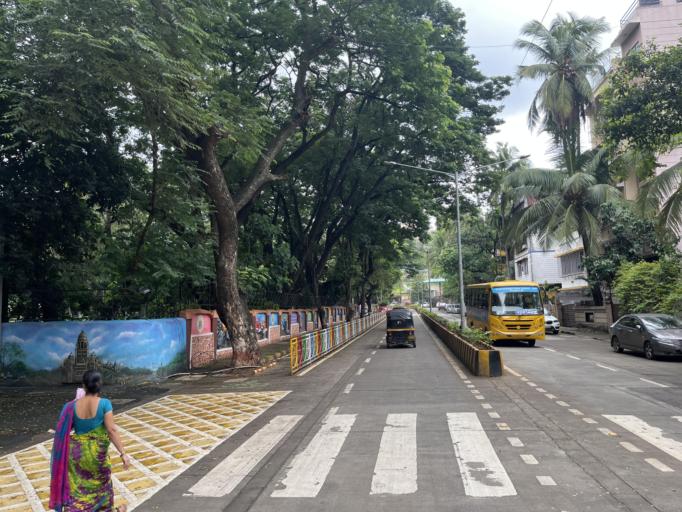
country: IN
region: Maharashtra
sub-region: Mumbai Suburban
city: Borivli
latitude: 19.2319
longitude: 72.8684
